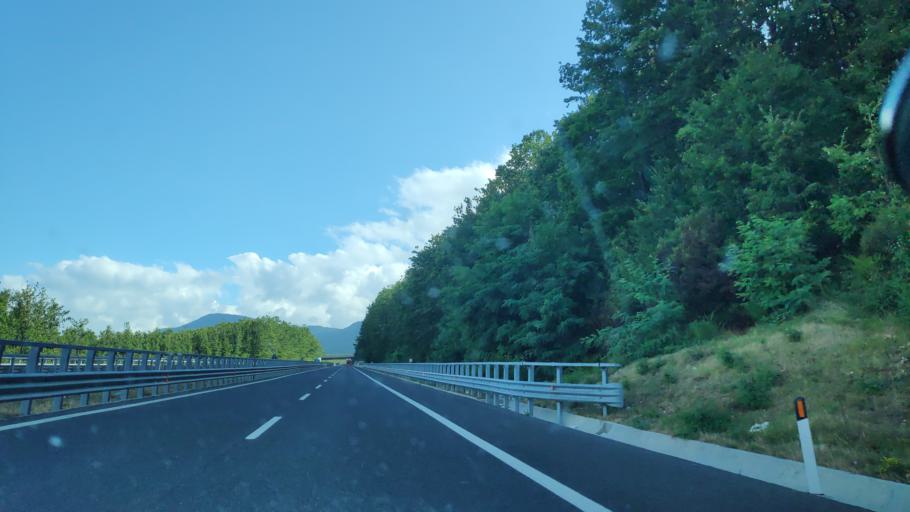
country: IT
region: Campania
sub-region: Provincia di Salerno
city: Buonabitacolo
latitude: 40.2510
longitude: 15.6599
